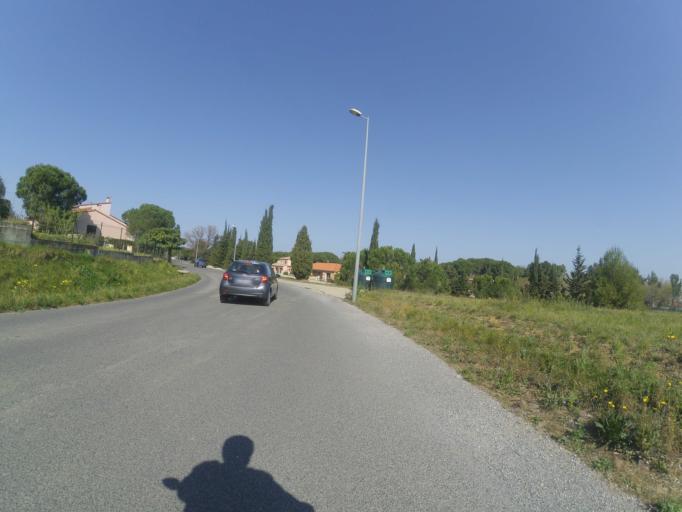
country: FR
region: Languedoc-Roussillon
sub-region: Departement des Pyrenees-Orientales
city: Thuir
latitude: 42.6271
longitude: 2.7619
